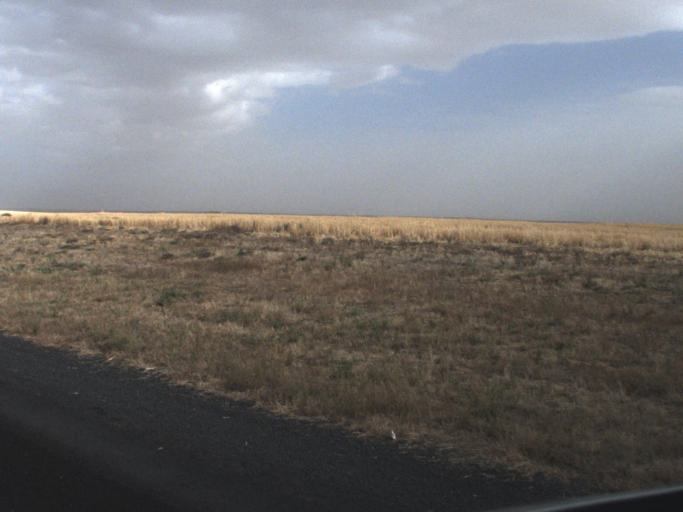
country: US
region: Washington
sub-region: Lincoln County
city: Davenport
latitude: 47.4321
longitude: -118.3381
